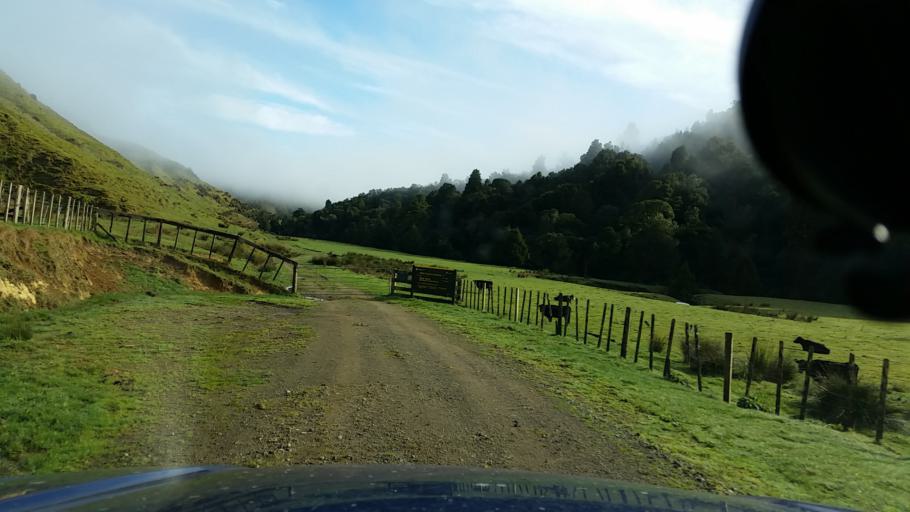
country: NZ
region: Taranaki
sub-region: New Plymouth District
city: Waitara
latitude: -38.9775
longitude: 174.7479
